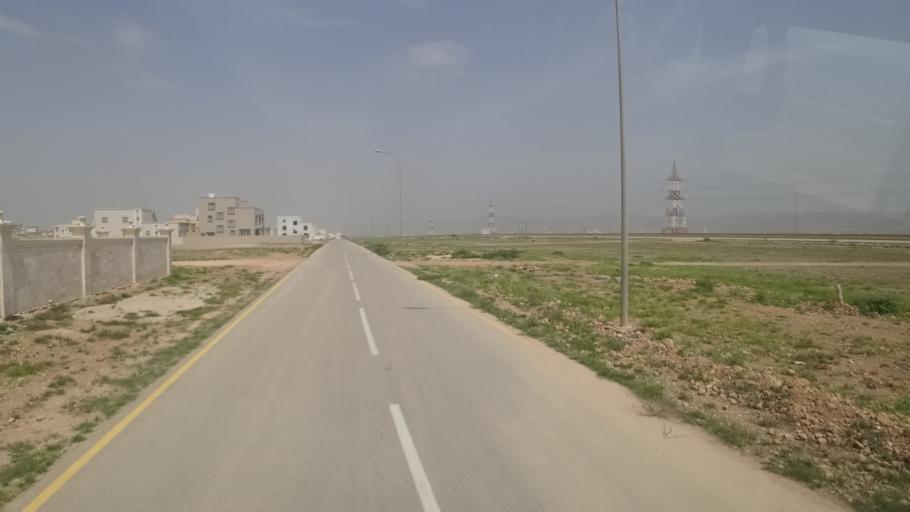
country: OM
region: Zufar
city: Salalah
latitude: 17.1027
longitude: 54.2142
